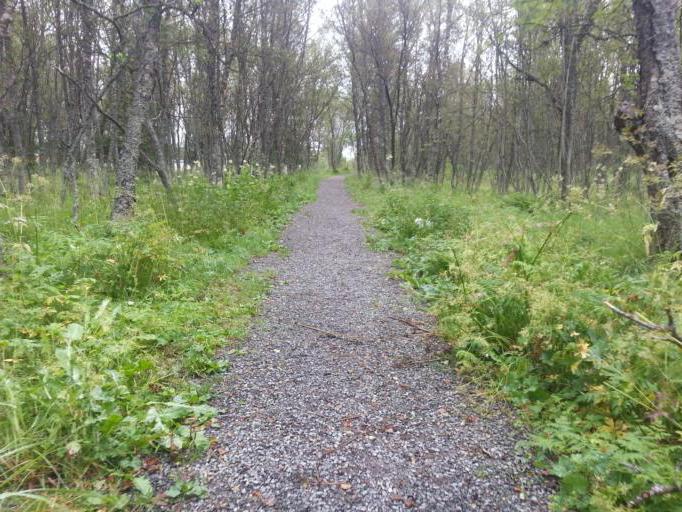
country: NO
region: Troms
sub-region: Tromso
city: Tromso
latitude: 69.6388
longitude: 18.9030
